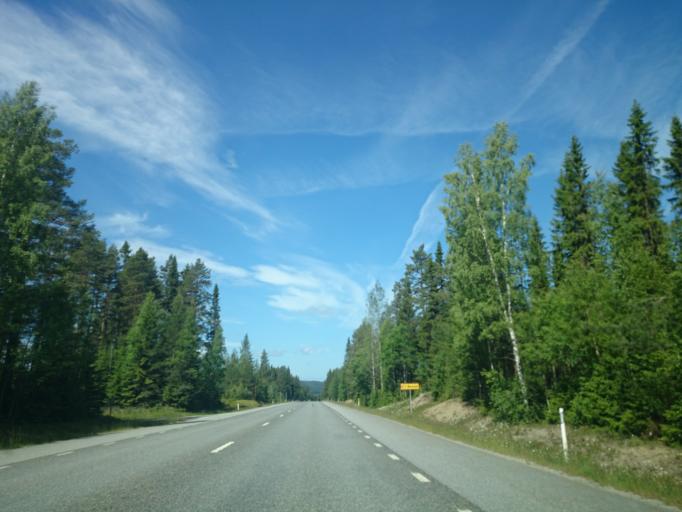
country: SE
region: Jaemtland
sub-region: Braecke Kommun
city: Braecke
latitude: 62.7114
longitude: 15.4752
